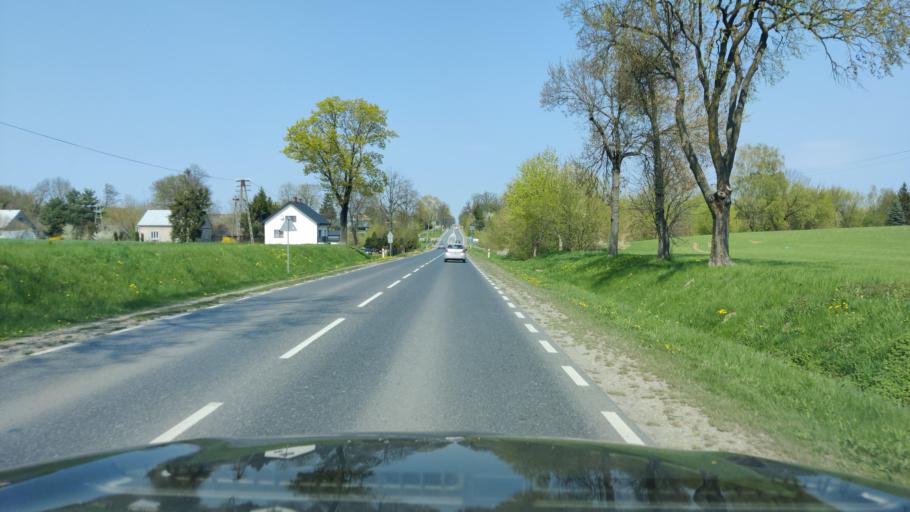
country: PL
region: Masovian Voivodeship
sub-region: Powiat pultuski
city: Pultusk
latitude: 52.6656
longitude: 21.0816
